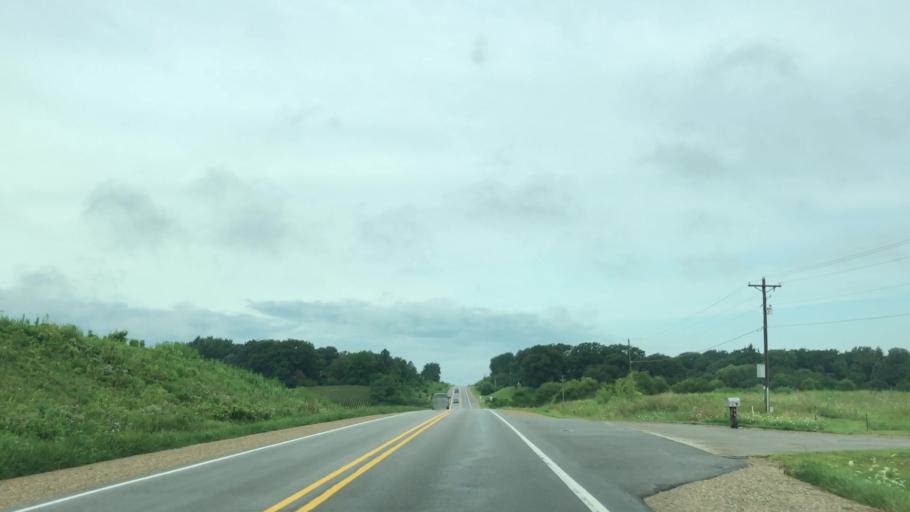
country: US
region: Iowa
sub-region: Marshall County
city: Marshalltown
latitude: 42.0075
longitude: -92.9431
